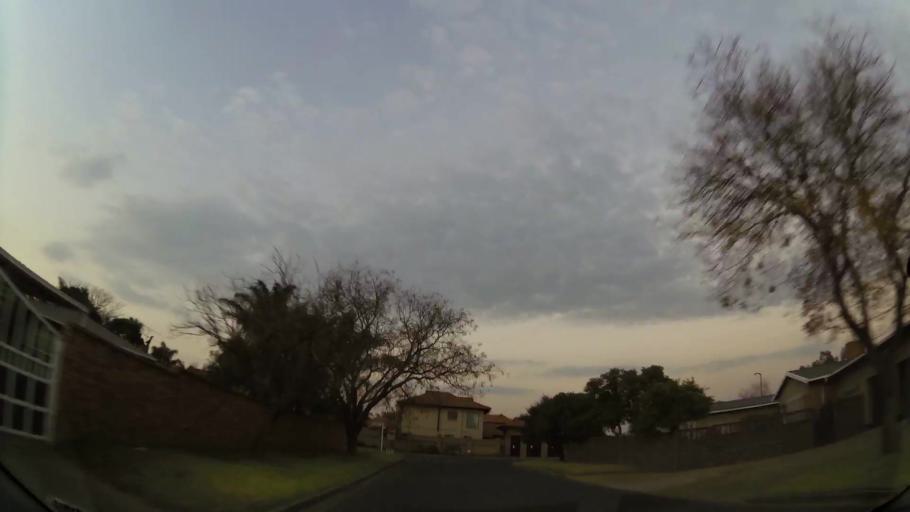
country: ZA
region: Gauteng
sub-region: Ekurhuleni Metropolitan Municipality
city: Benoni
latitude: -26.1455
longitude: 28.3030
